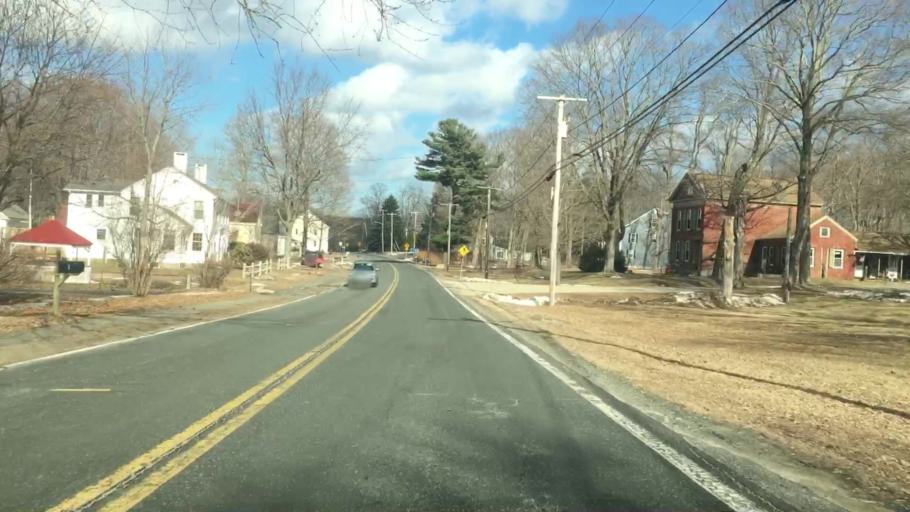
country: US
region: Massachusetts
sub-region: Hampden County
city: Wales
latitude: 42.0657
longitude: -72.2227
